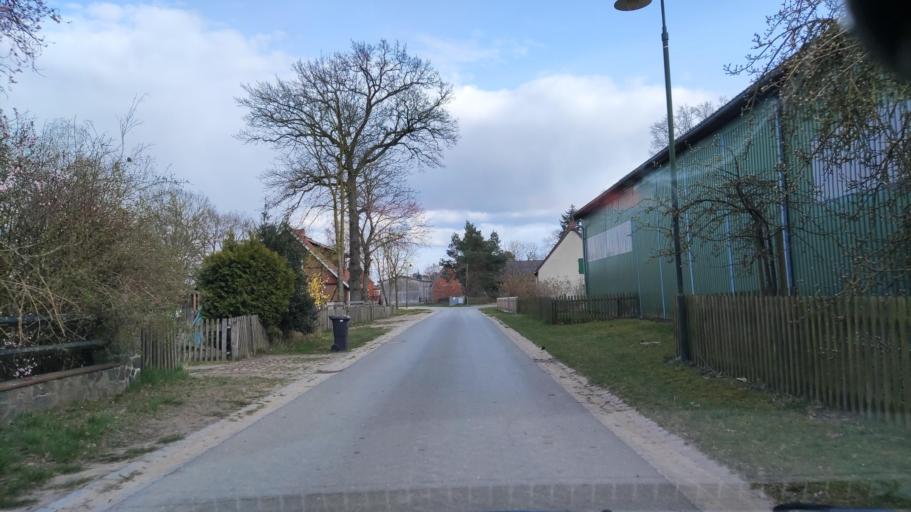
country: DE
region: Lower Saxony
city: Langendorf
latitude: 53.1083
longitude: 11.2351
